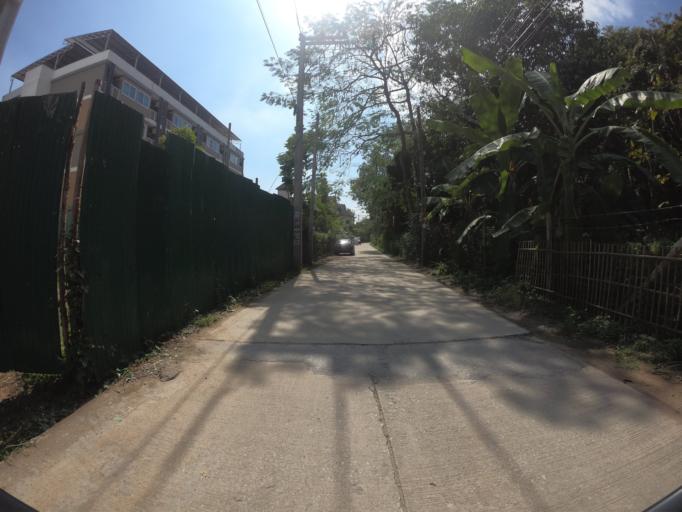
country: TH
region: Chiang Mai
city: Chiang Mai
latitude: 18.7870
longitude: 98.9573
